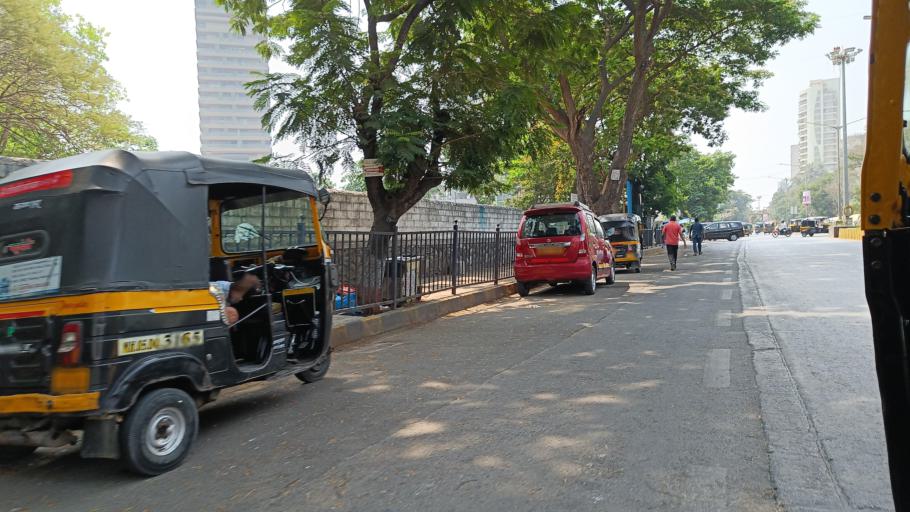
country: IN
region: Maharashtra
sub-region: Mumbai Suburban
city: Powai
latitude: 19.1366
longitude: 72.8257
